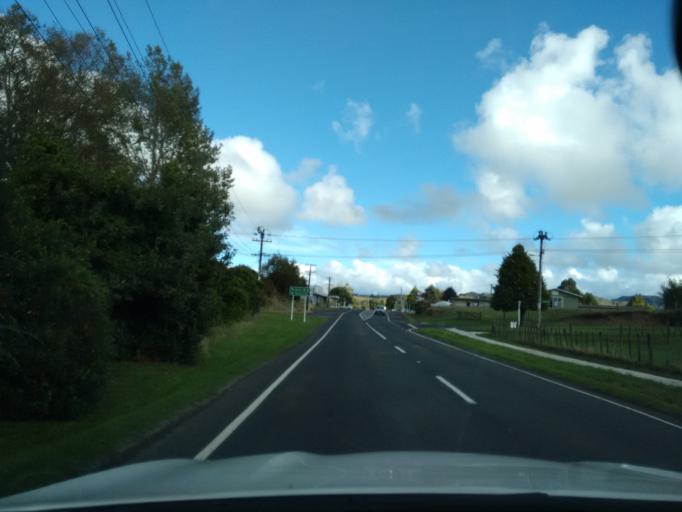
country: NZ
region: Manawatu-Wanganui
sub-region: Ruapehu District
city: Waiouru
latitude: -39.4259
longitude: 175.2818
